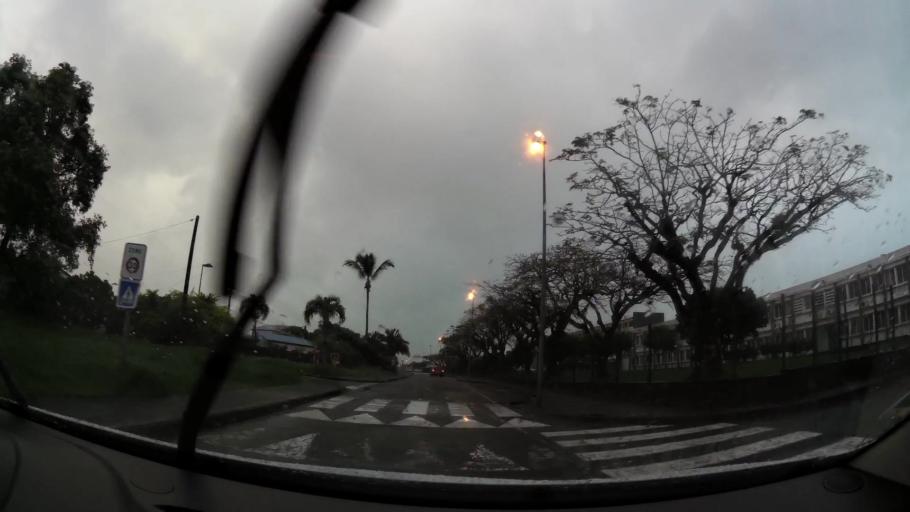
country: RE
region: Reunion
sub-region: Reunion
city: Saint-Benoit
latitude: -21.0405
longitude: 55.7171
